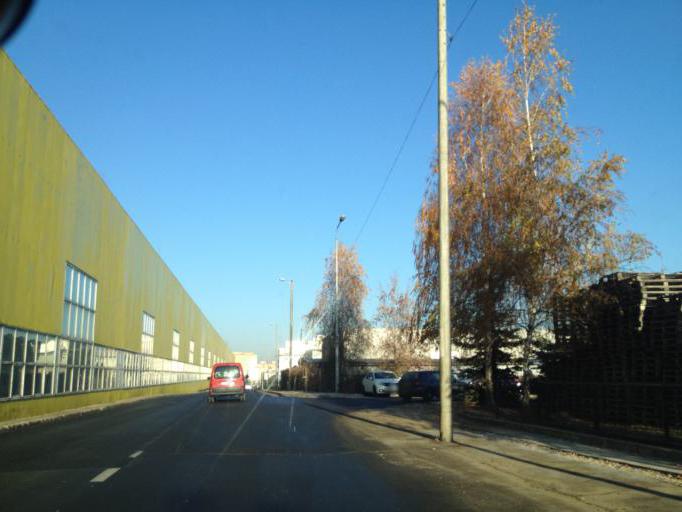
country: RO
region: Brasov
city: Brasov
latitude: 45.6301
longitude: 25.6364
